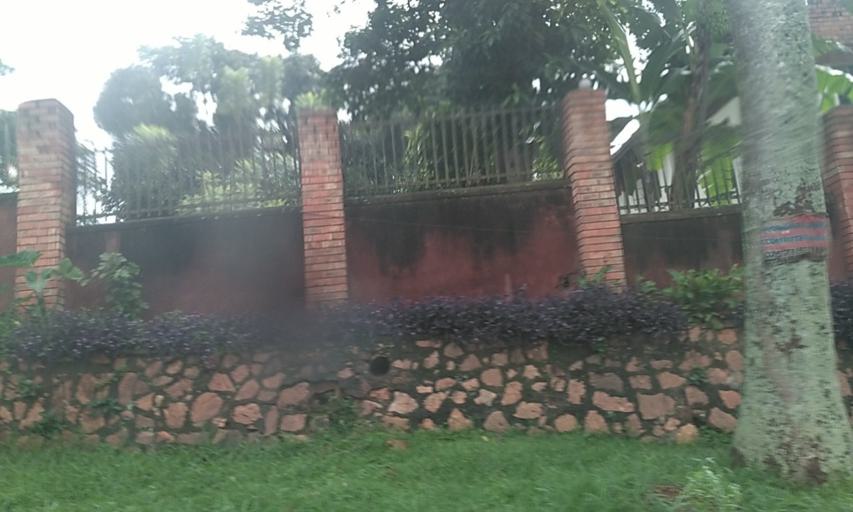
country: UG
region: Central Region
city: Kampala Central Division
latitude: 0.3284
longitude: 32.5864
